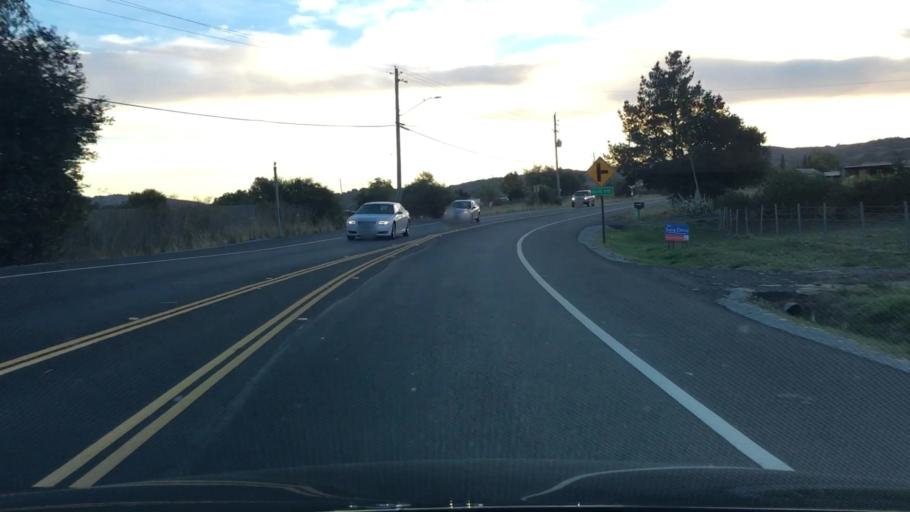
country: US
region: California
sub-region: Sonoma County
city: El Verano
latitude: 38.2905
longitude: -122.4886
